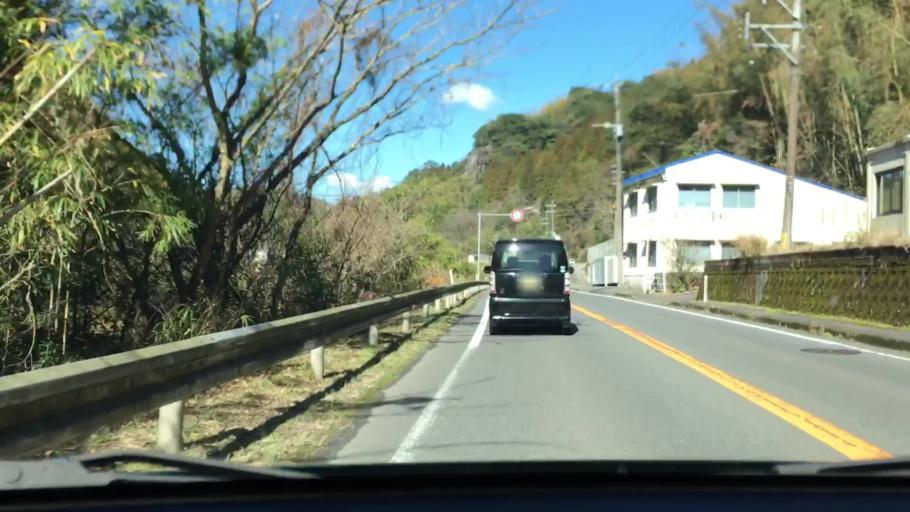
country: JP
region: Kagoshima
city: Kagoshima-shi
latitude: 31.6466
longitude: 130.5141
